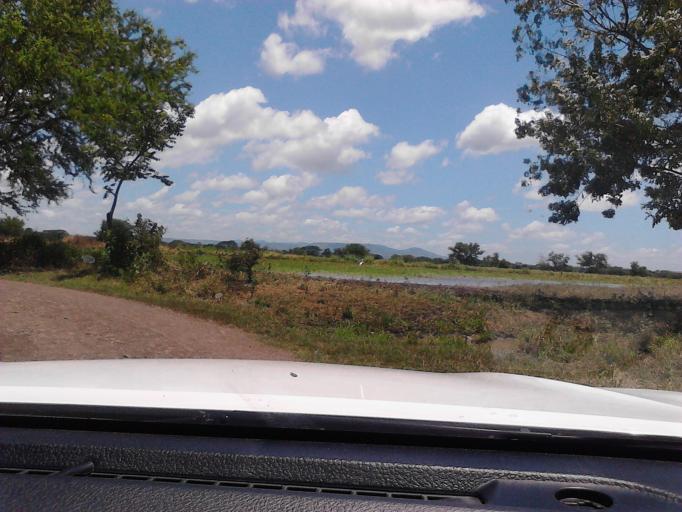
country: NI
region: Matagalpa
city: Ciudad Dario
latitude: 12.9072
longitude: -86.1407
